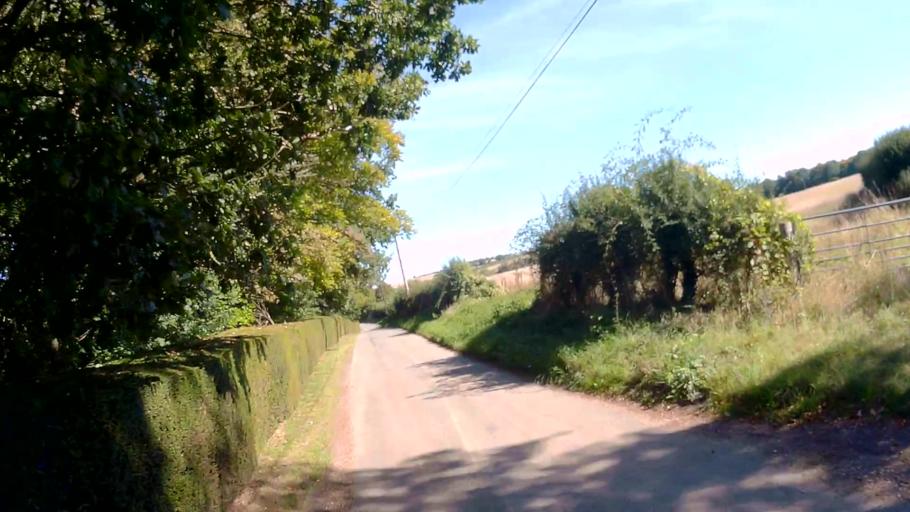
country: GB
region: England
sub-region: Hampshire
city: Andover
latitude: 51.1613
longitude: -1.4174
